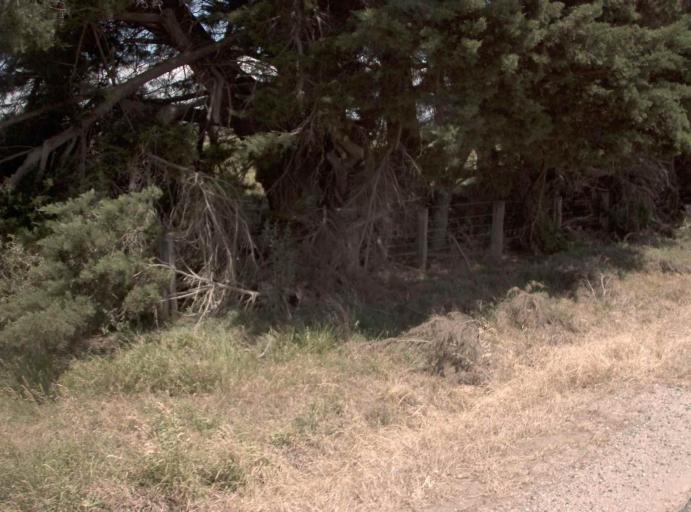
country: AU
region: Victoria
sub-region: Wellington
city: Heyfield
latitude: -38.0192
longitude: 146.8817
